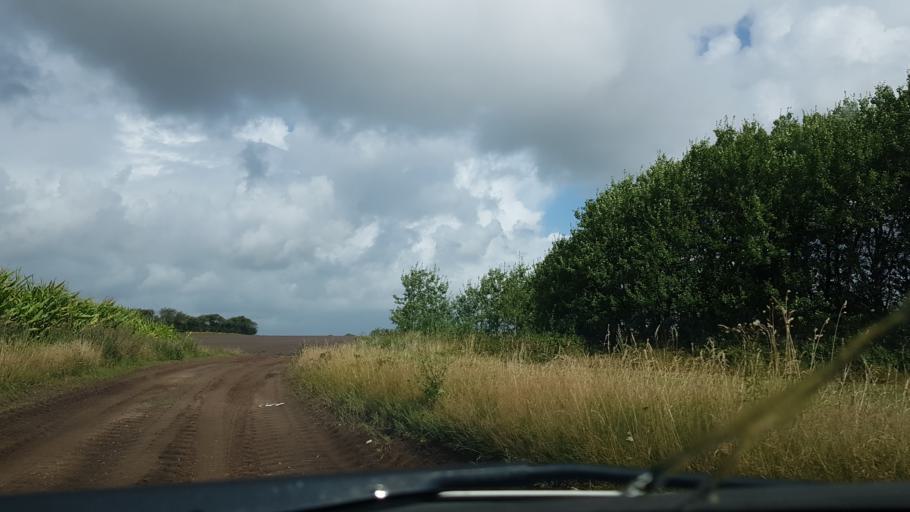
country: DK
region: South Denmark
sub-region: Esbjerg Kommune
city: Ribe
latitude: 55.2558
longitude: 8.7612
